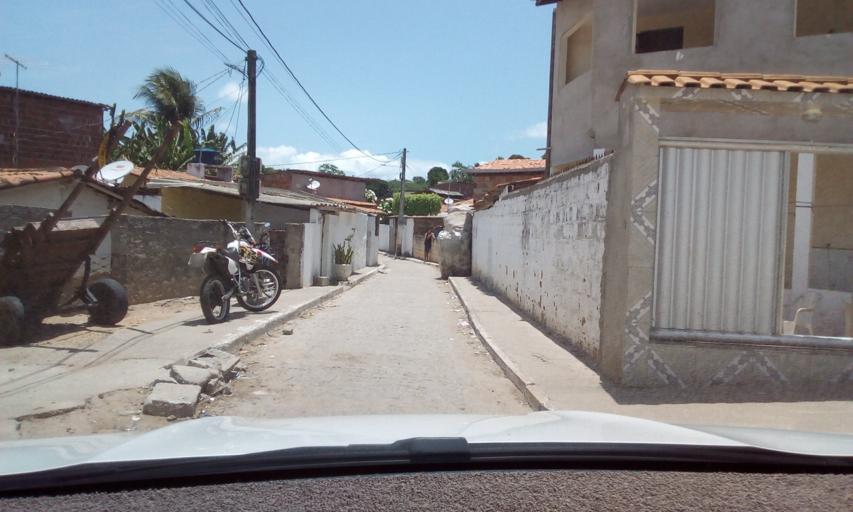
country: BR
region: Paraiba
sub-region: Joao Pessoa
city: Joao Pessoa
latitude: -7.1469
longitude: -34.8290
